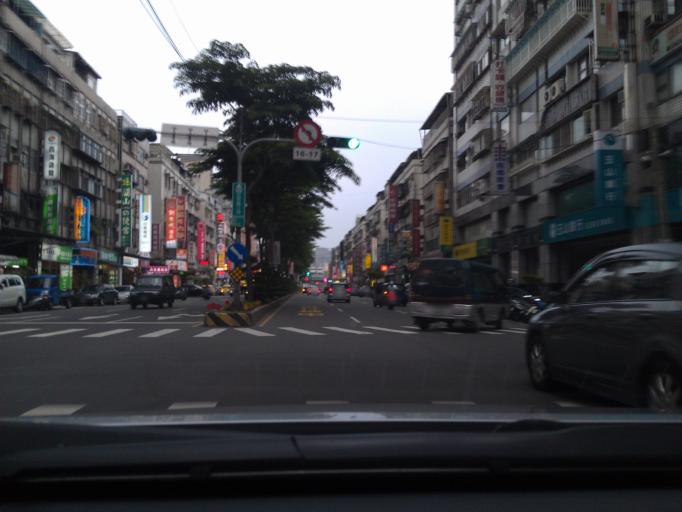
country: TW
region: Taipei
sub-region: Taipei
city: Banqiao
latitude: 25.0151
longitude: 121.4790
